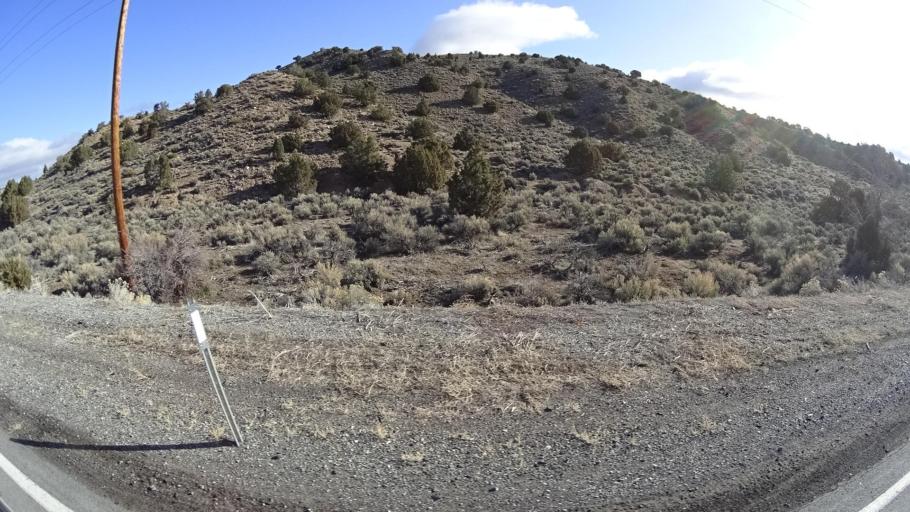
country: US
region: Nevada
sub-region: Washoe County
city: Lemmon Valley
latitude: 39.7345
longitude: -119.8823
